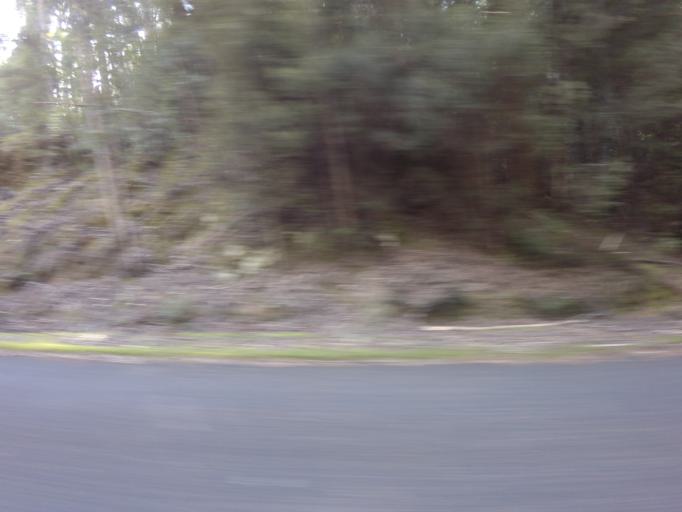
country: AU
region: Tasmania
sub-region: Huon Valley
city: Geeveston
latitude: -42.8268
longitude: 146.3237
